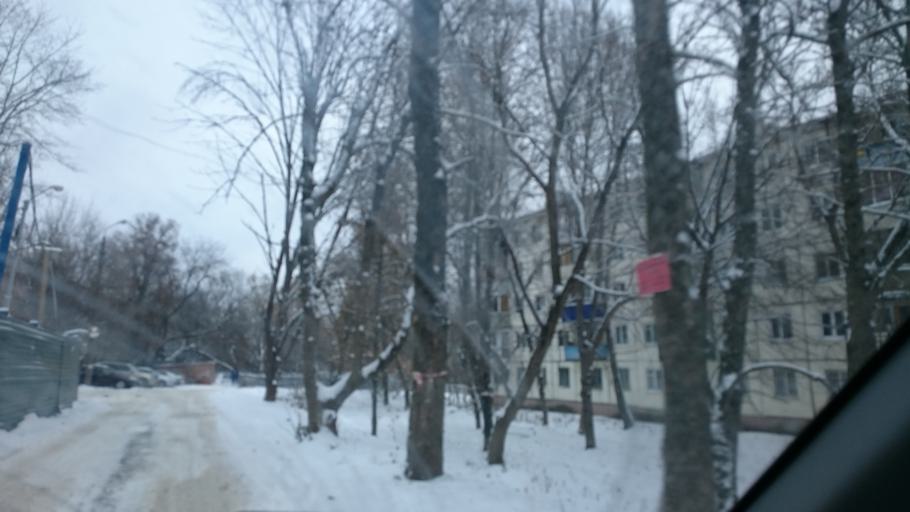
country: RU
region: Tula
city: Mendeleyevskiy
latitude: 54.1540
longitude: 37.5901
